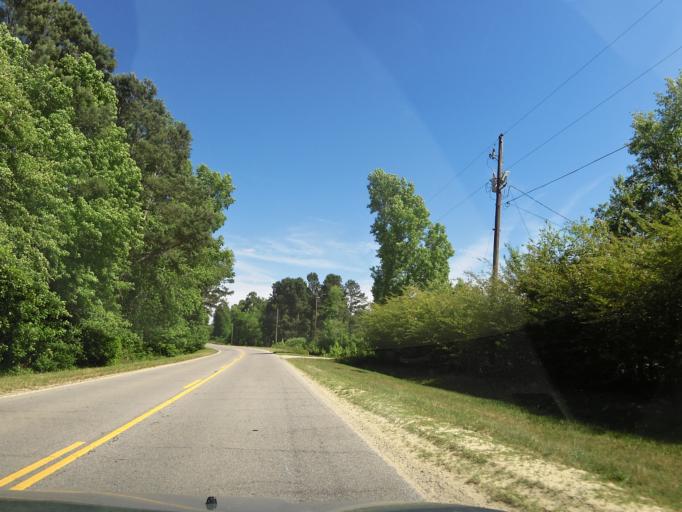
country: US
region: South Carolina
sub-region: Barnwell County
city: Williston
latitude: 33.3883
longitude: -81.3966
